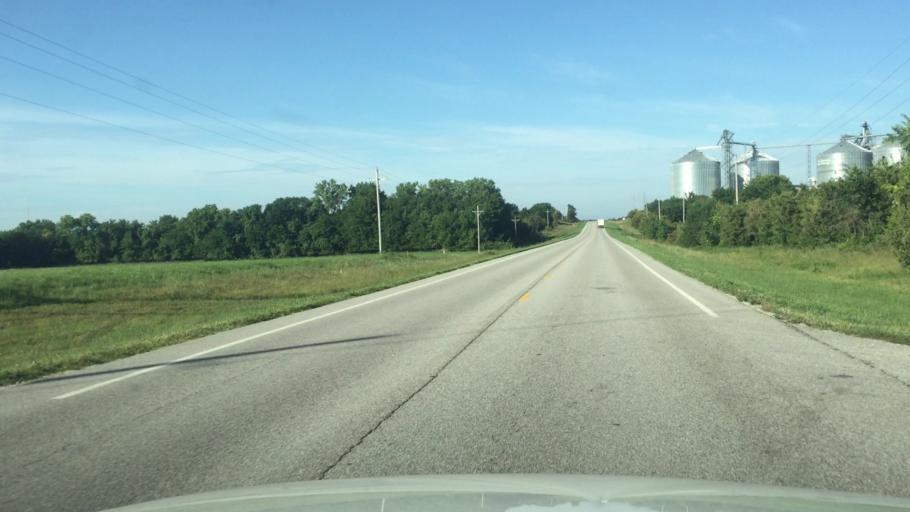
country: US
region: Kansas
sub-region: Anderson County
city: Garnett
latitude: 38.2735
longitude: -95.2314
